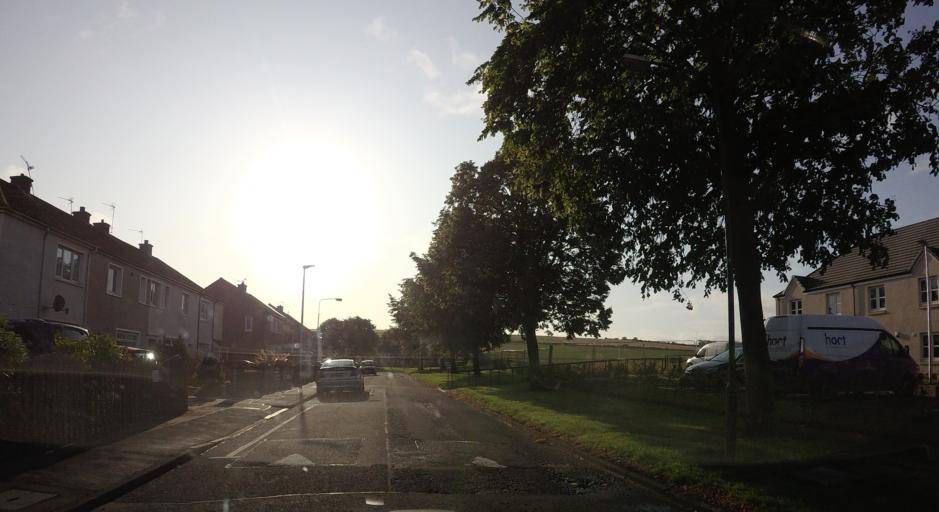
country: GB
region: Scotland
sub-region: East Lothian
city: Musselburgh
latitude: 55.9332
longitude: -3.0137
